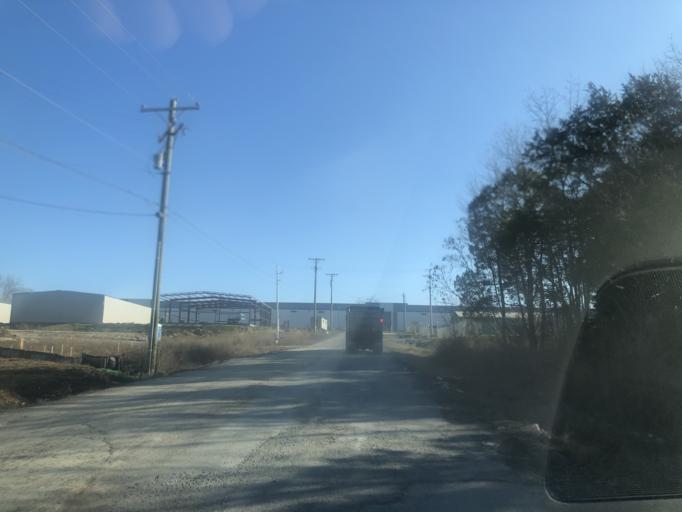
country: US
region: Tennessee
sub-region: Rutherford County
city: La Vergne
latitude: 36.0063
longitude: -86.5891
